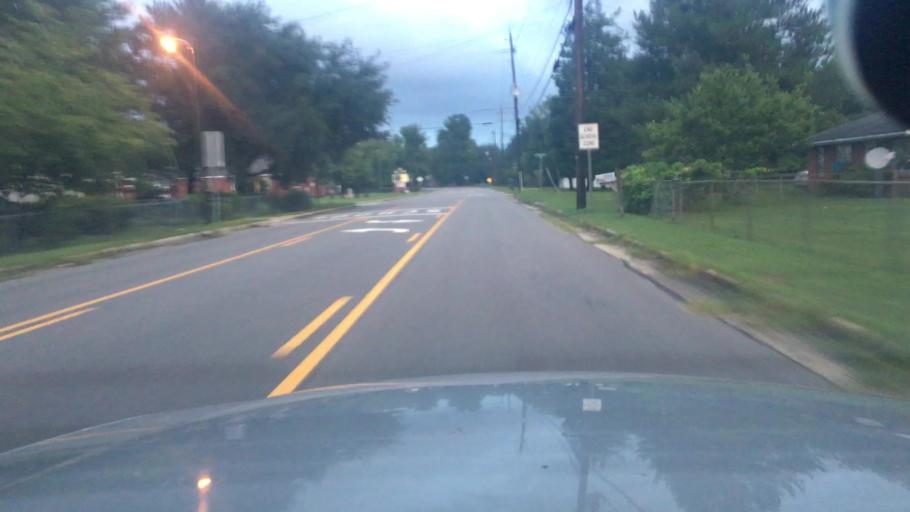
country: US
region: North Carolina
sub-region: Cumberland County
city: Hope Mills
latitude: 34.9659
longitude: -78.9369
